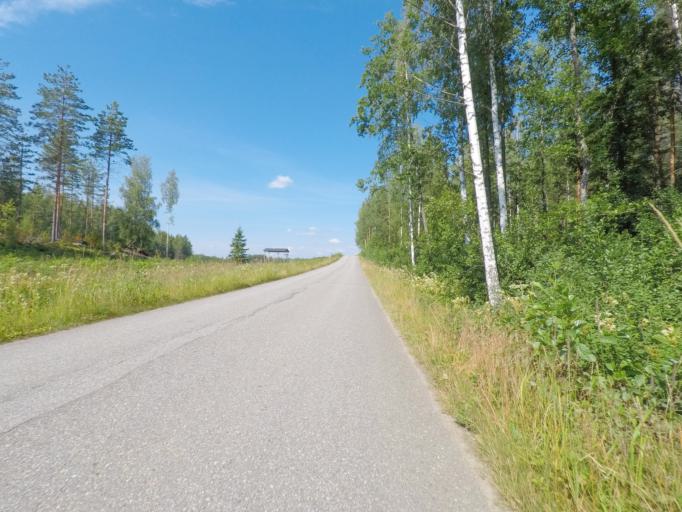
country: FI
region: Southern Savonia
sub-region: Mikkeli
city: Puumala
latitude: 61.4125
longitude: 28.0923
